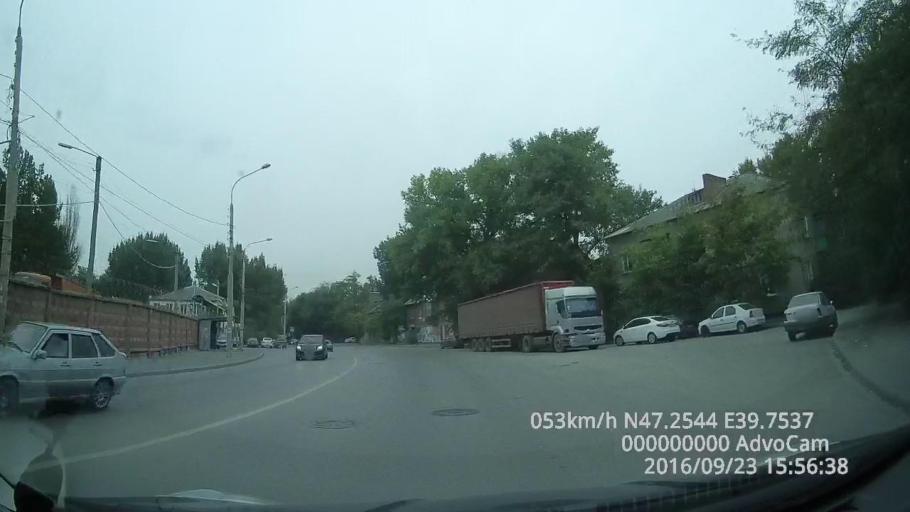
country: RU
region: Rostov
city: Imeni Chkalova
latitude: 47.2545
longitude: 39.7536
